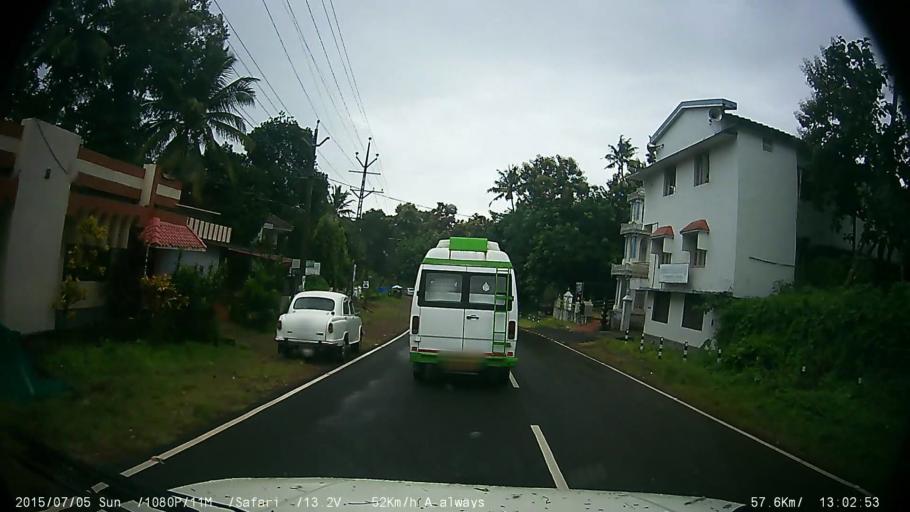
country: IN
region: Kerala
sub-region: Kottayam
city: Changanacheri
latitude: 9.4934
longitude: 76.5731
